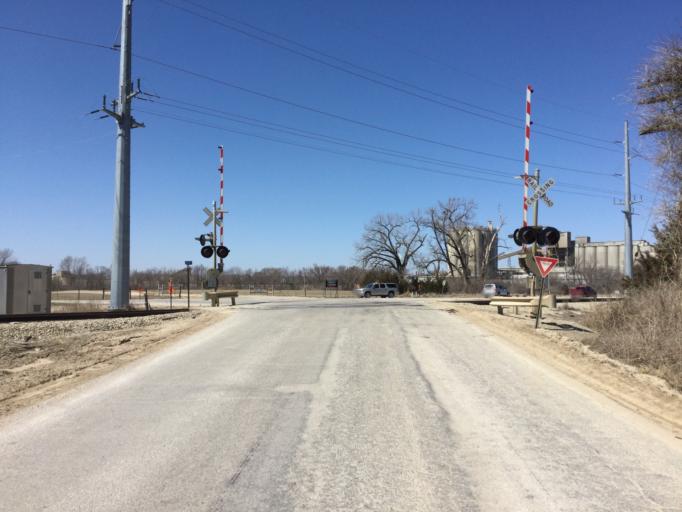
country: US
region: Kansas
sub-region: Allen County
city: Humboldt
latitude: 37.7919
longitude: -95.4287
